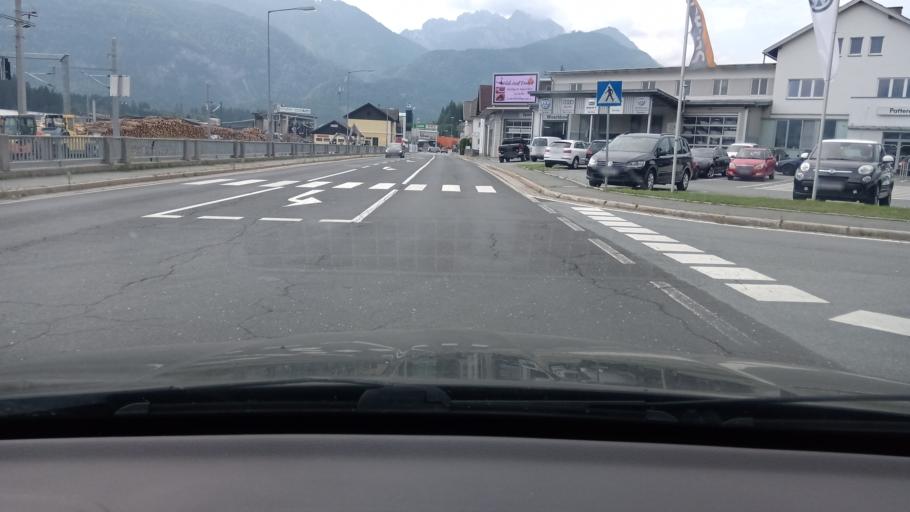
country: AT
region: Carinthia
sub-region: Politischer Bezirk Hermagor
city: Hermagor
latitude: 46.6280
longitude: 13.3767
